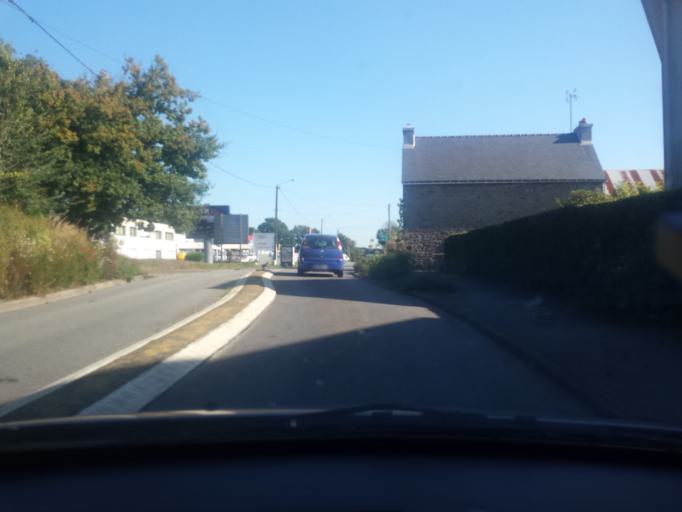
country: FR
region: Brittany
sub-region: Departement du Morbihan
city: Pontivy
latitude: 48.0611
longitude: -2.9568
